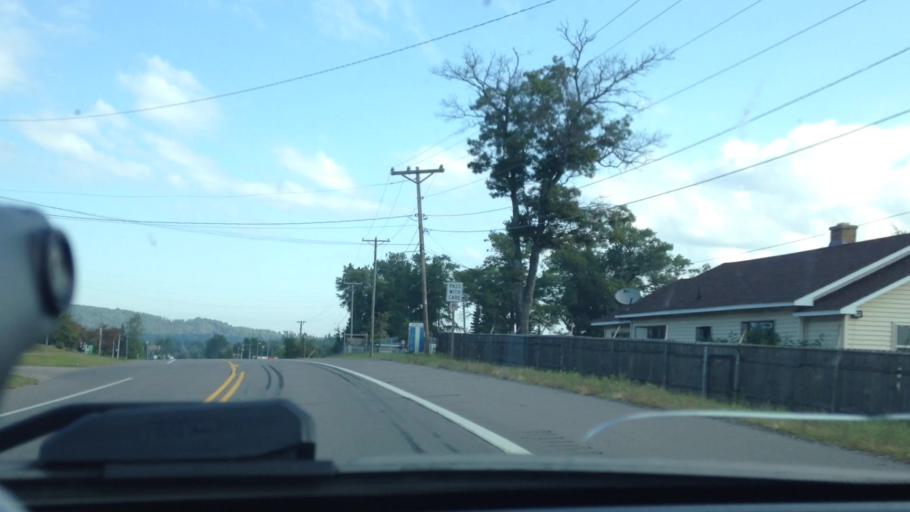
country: US
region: Michigan
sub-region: Dickinson County
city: Norway
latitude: 45.7714
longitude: -87.9090
